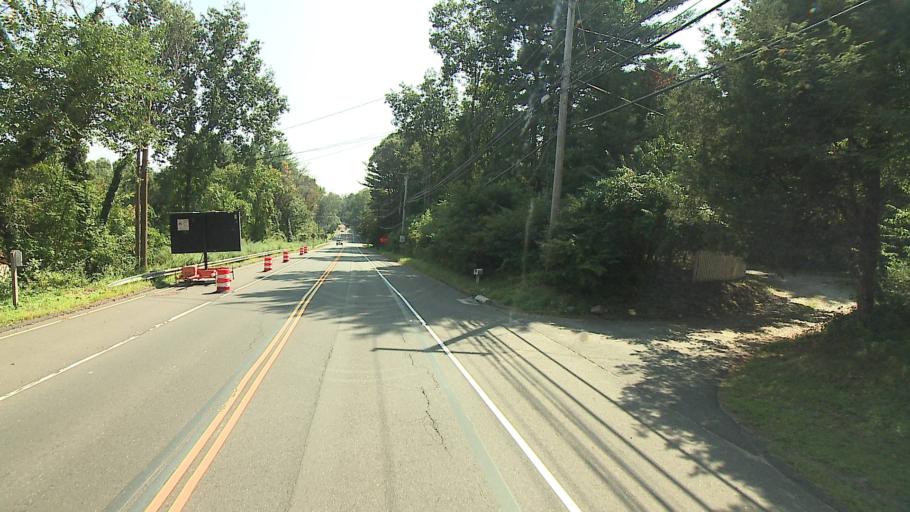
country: US
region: Connecticut
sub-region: Fairfield County
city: Westport
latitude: 41.1863
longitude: -73.3699
